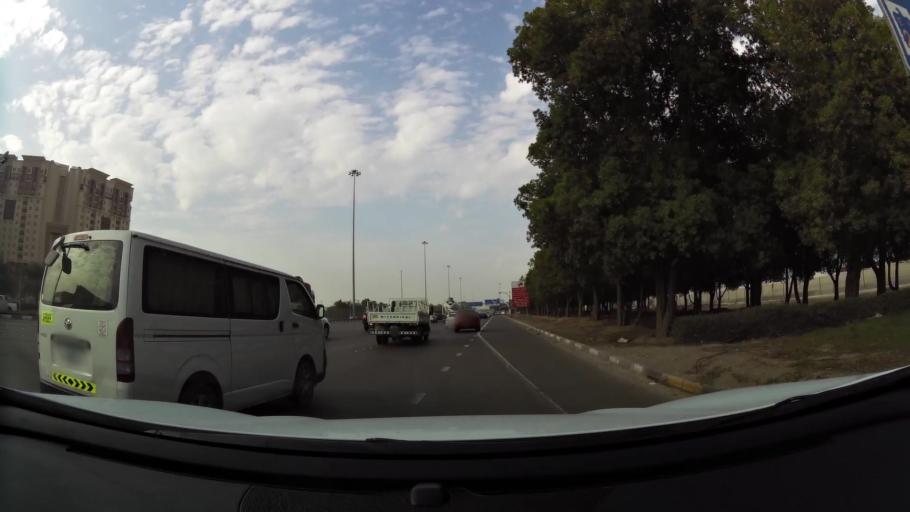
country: AE
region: Abu Dhabi
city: Abu Dhabi
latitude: 24.3839
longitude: 54.5246
